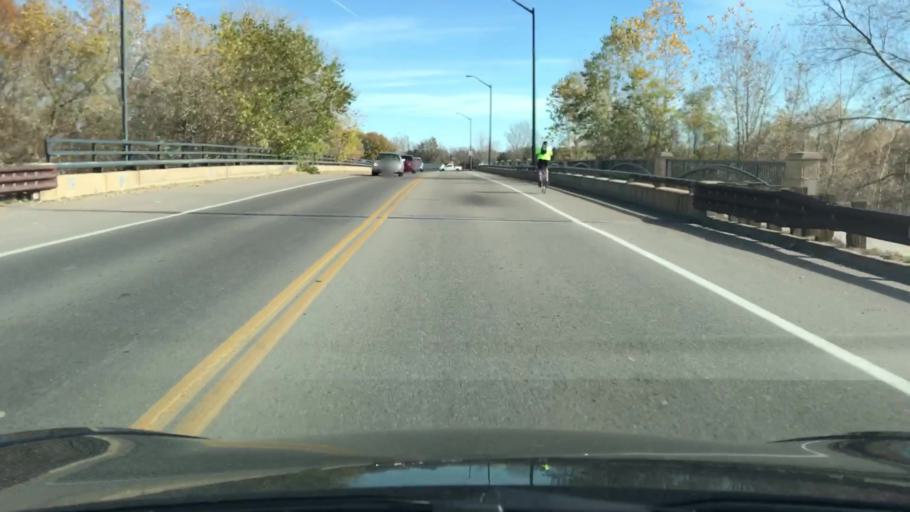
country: US
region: Colorado
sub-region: Larimer County
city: Fort Collins
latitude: 40.5778
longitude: -105.0360
